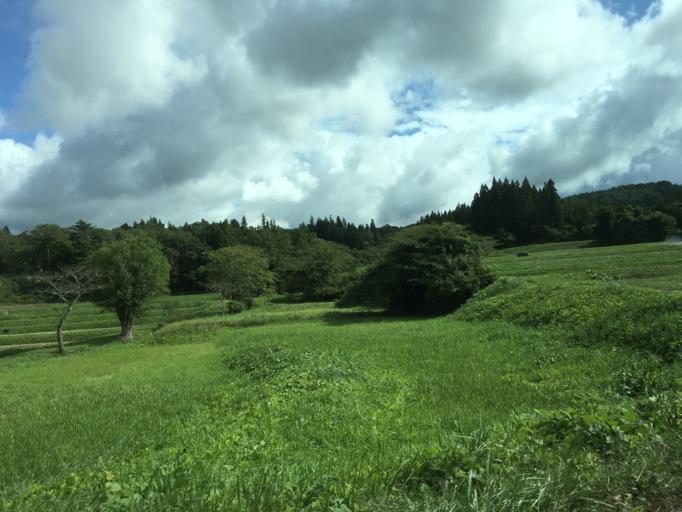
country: JP
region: Iwate
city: Ichinoseki
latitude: 38.8334
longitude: 141.3570
